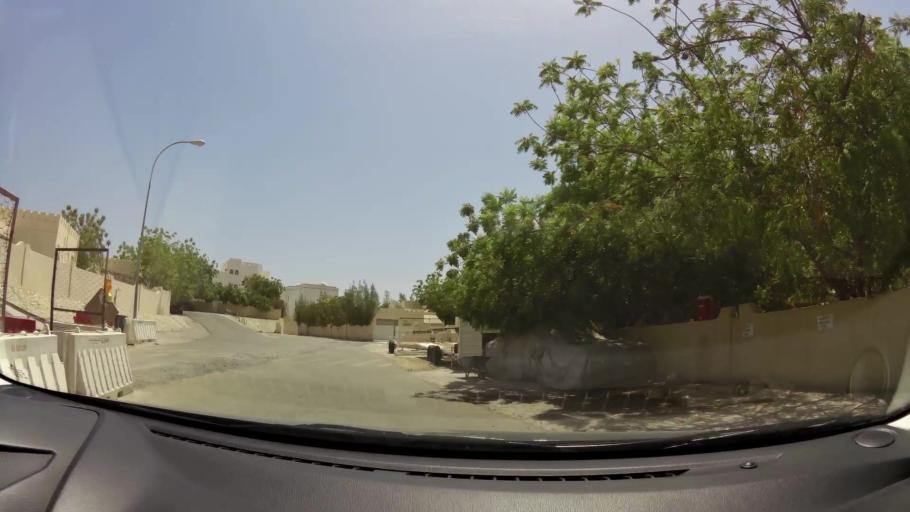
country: OM
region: Muhafazat Masqat
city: Bawshar
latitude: 23.5841
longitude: 58.4475
